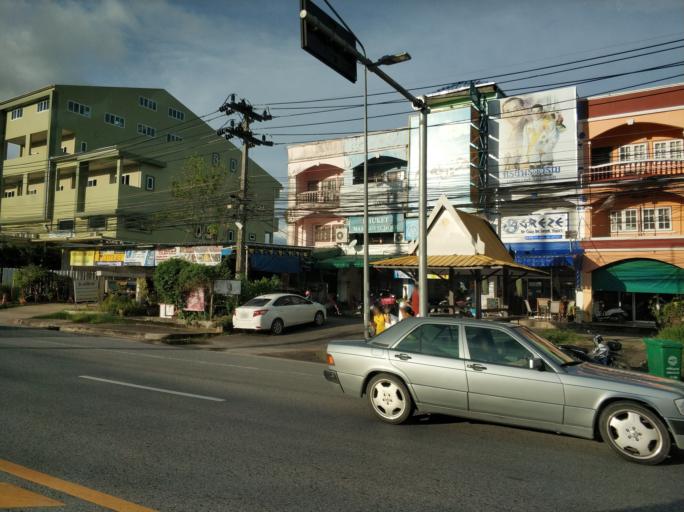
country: TH
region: Phuket
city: Wichit
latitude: 7.8946
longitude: 98.3648
